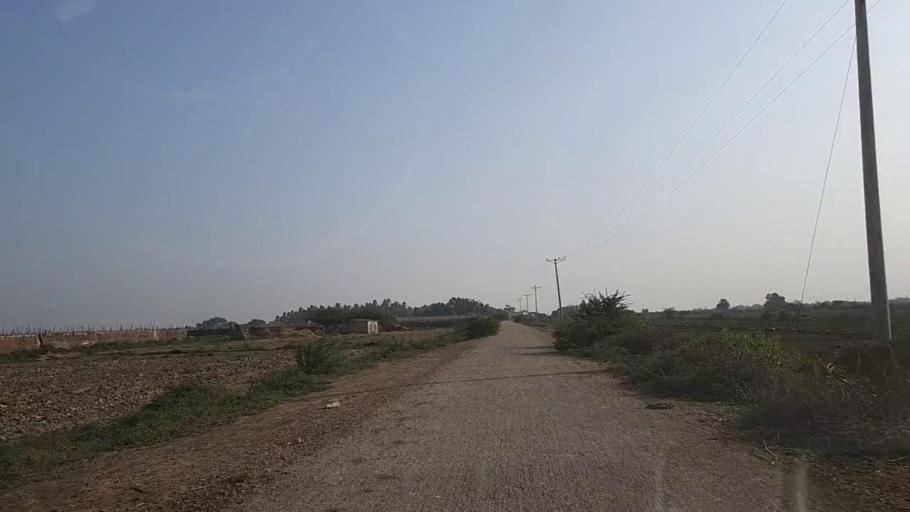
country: PK
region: Sindh
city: Keti Bandar
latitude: 24.1688
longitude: 67.6261
